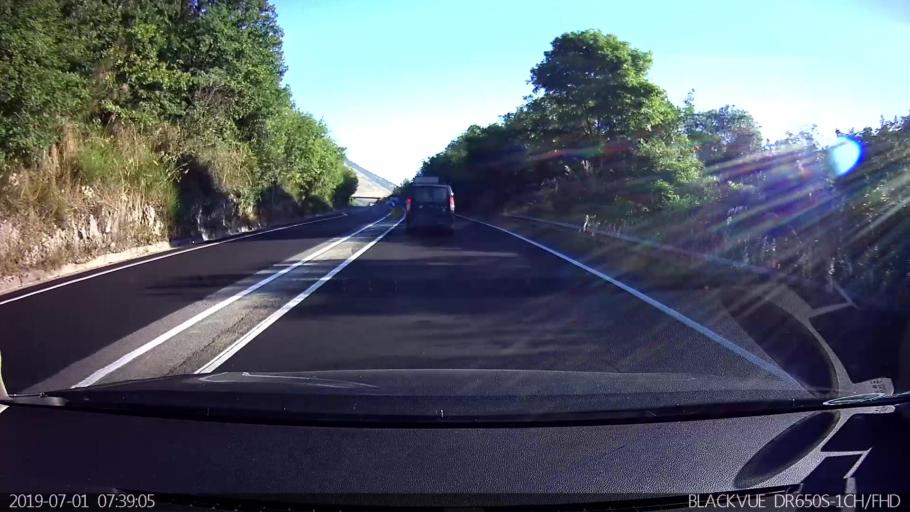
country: IT
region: Latium
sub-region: Provincia di Frosinone
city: Giuliano di Roma
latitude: 41.5472
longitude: 13.2695
